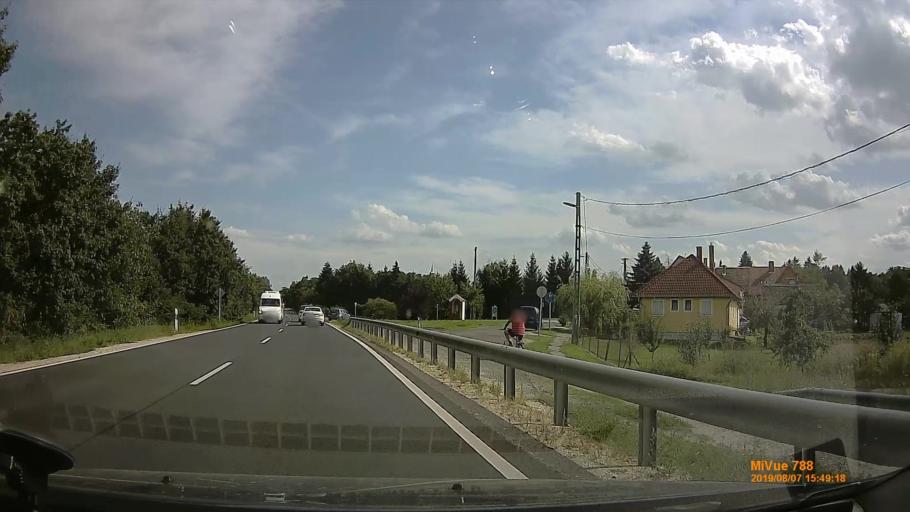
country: HU
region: Vas
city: Jak
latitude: 47.1511
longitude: 16.6408
